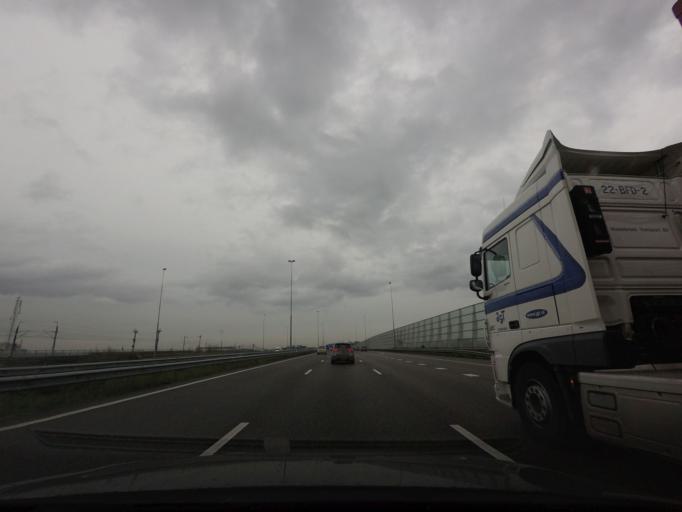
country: NL
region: North Brabant
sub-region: Gemeente Breda
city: Breda
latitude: 51.5924
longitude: 4.7236
